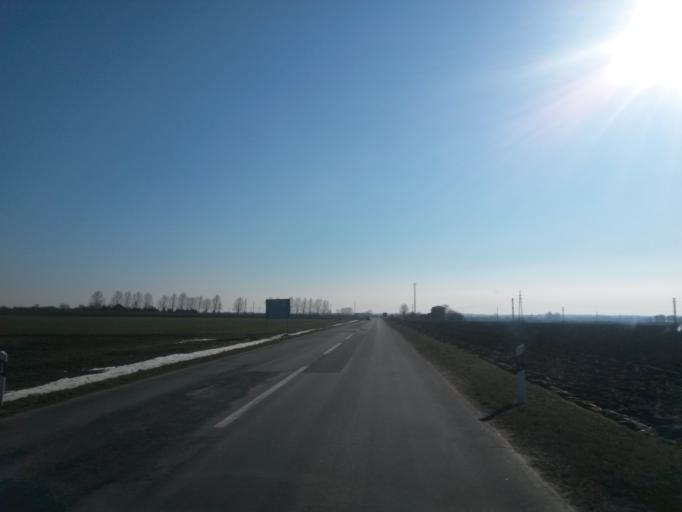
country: HR
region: Osjecko-Baranjska
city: Dalj
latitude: 45.5049
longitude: 18.9484
